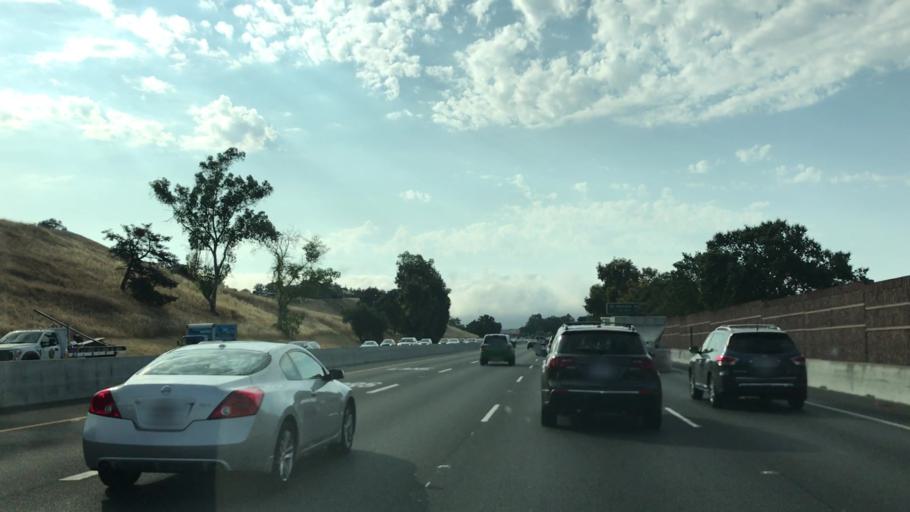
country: US
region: California
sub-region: Contra Costa County
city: Alamo
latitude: 37.8441
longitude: -122.0235
